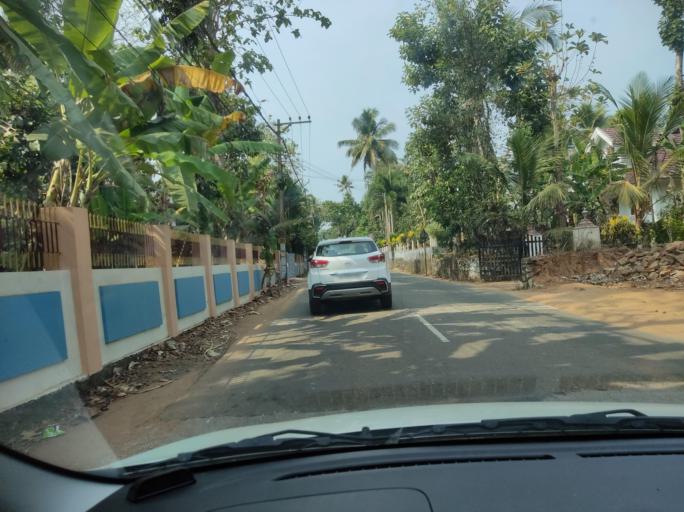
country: IN
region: Kerala
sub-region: Kottayam
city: Kottayam
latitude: 9.6830
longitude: 76.5057
